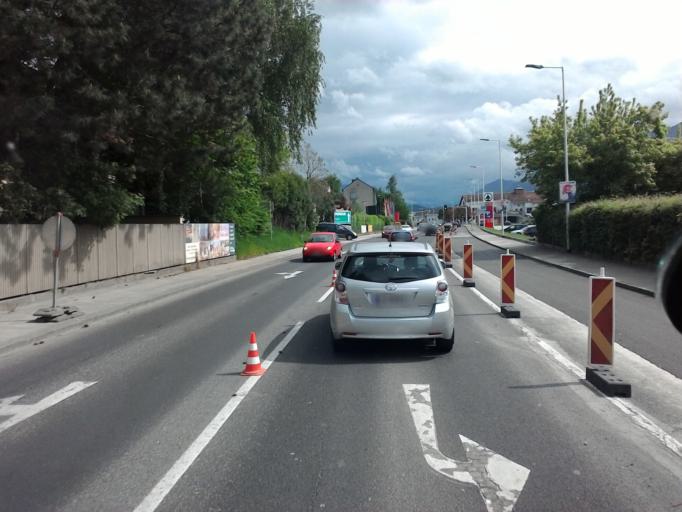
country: AT
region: Upper Austria
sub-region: Politischer Bezirk Kirchdorf an der Krems
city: Micheldorf in Oberoesterreich
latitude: 47.9081
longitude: 14.1188
